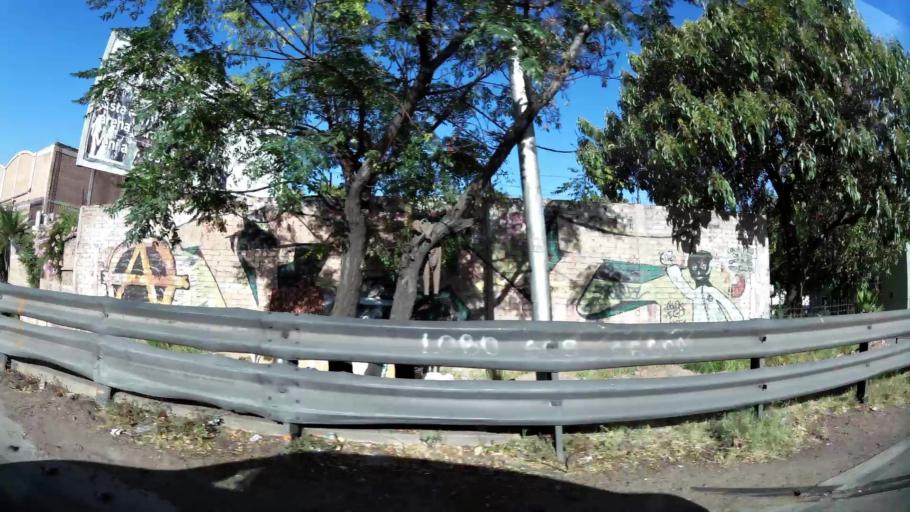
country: AR
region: Mendoza
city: Mendoza
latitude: -32.9060
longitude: -68.8383
